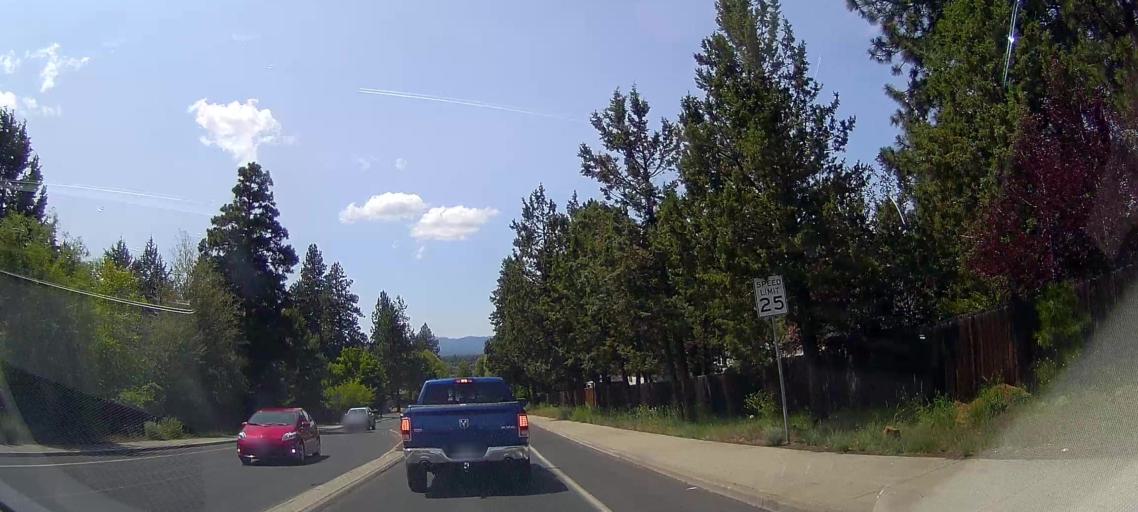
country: US
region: Oregon
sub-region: Deschutes County
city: Bend
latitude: 44.0392
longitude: -121.3106
